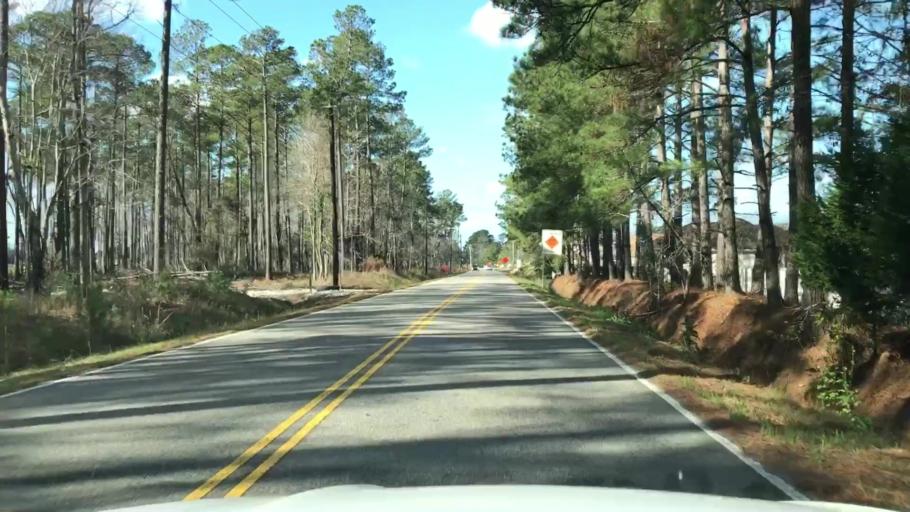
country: US
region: South Carolina
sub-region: Horry County
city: Socastee
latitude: 33.6584
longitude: -79.0021
